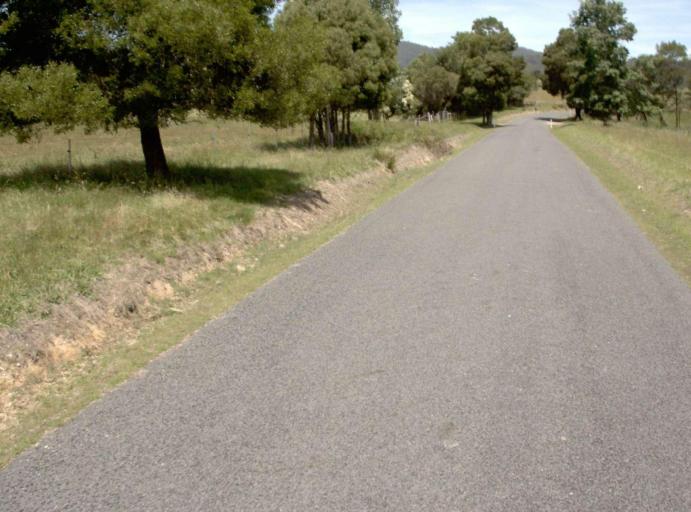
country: AU
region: New South Wales
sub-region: Bombala
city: Bombala
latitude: -37.4142
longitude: 149.0099
